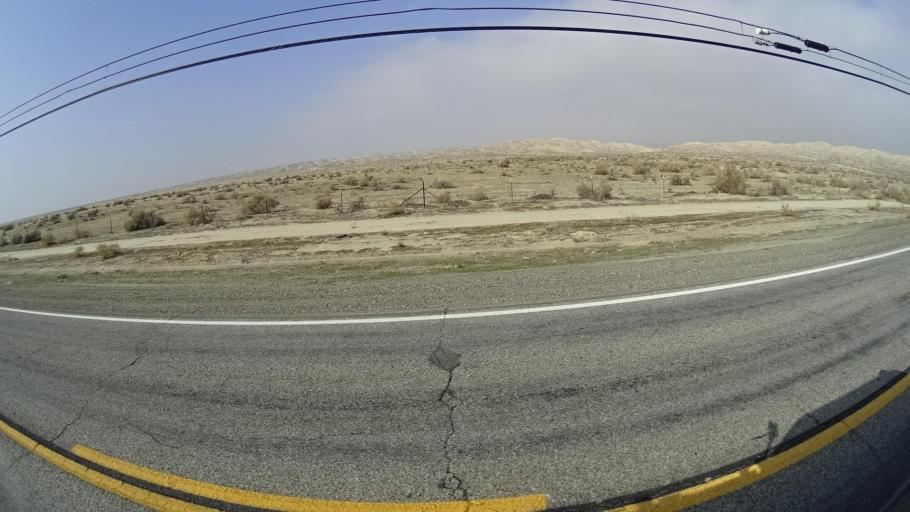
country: US
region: California
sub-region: Kern County
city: Ford City
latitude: 35.2278
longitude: -119.3779
